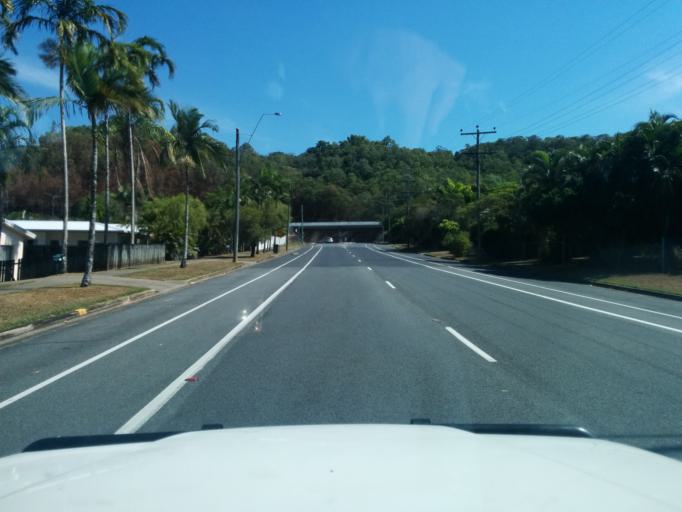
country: AU
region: Queensland
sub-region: Cairns
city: Cairns
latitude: -16.9129
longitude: 145.7279
